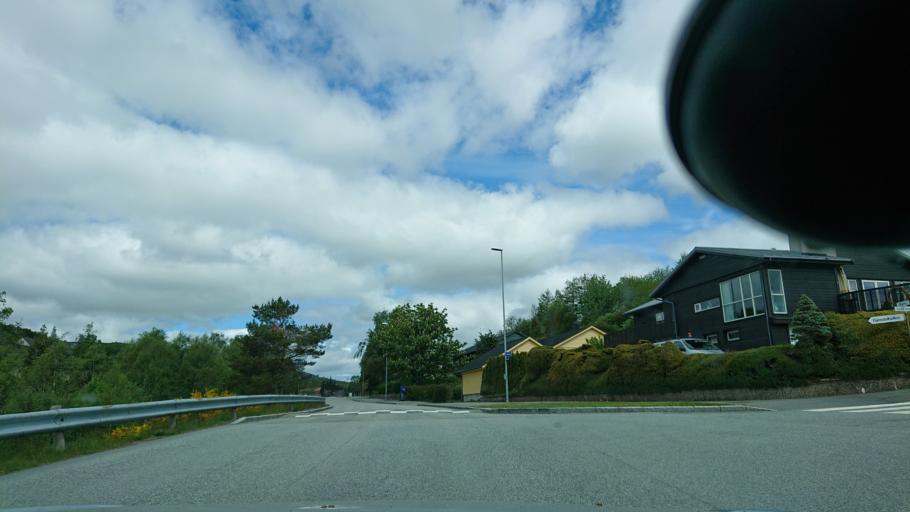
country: NO
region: Rogaland
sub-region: Gjesdal
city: Algard
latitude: 58.7695
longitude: 5.8654
